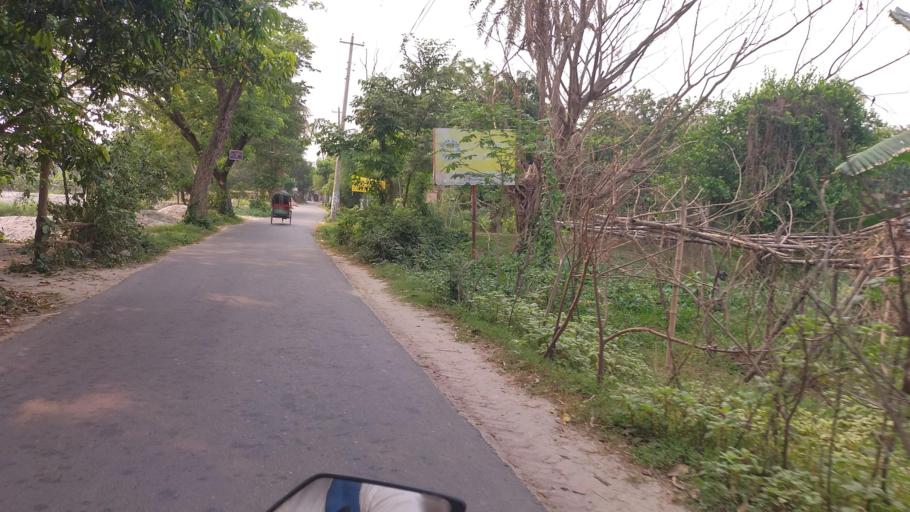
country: BD
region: Dhaka
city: Azimpur
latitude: 23.6699
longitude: 90.3454
